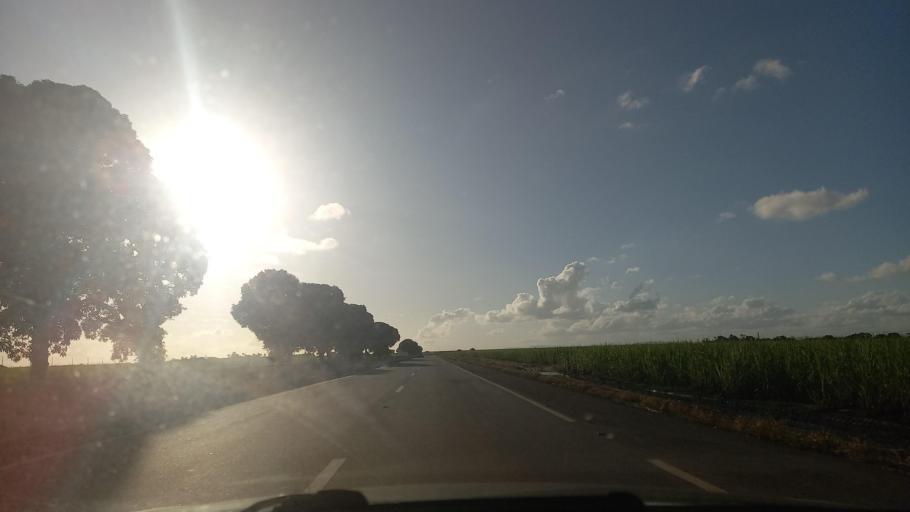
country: BR
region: Alagoas
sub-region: Campo Alegre
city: Campo Alegre
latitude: -9.8119
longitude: -36.2557
